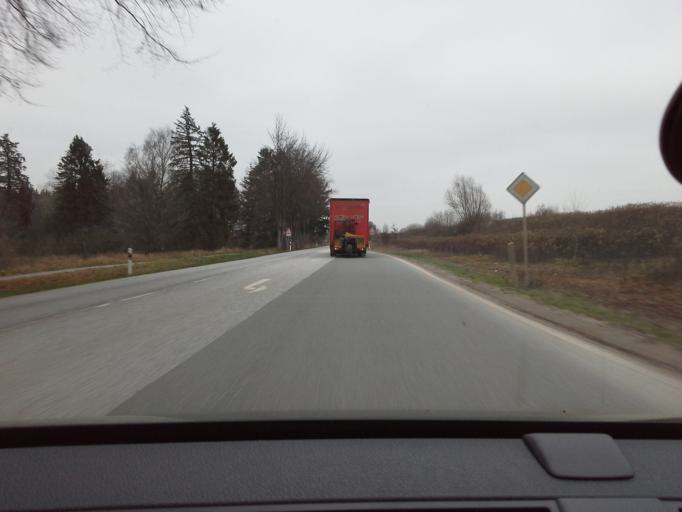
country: DE
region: Schleswig-Holstein
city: Lentfohrden
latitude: 53.8476
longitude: 9.8871
